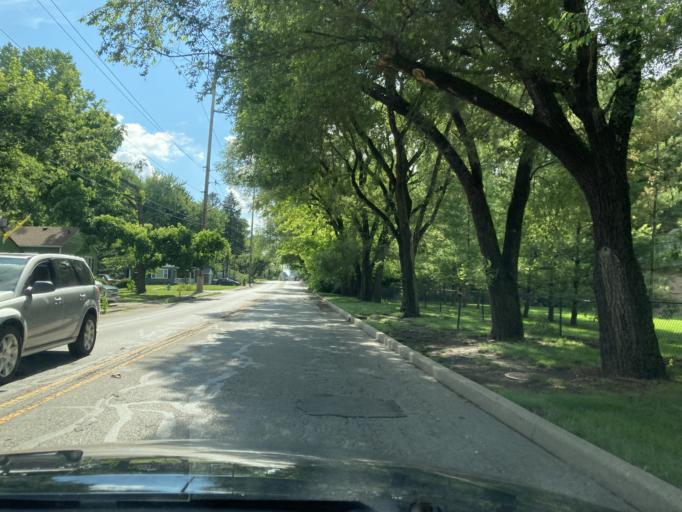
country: US
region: Indiana
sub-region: Marion County
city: Broad Ripple
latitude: 39.8513
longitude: -86.1307
